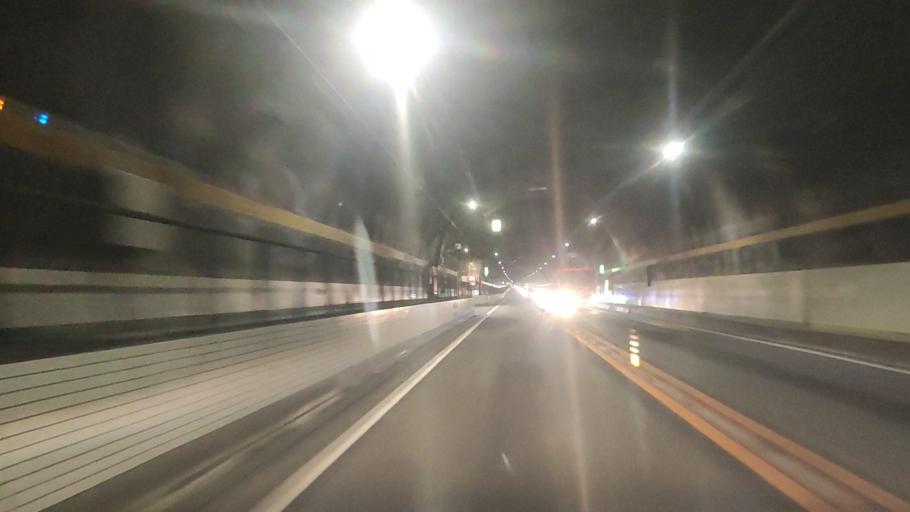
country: JP
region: Nagasaki
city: Obita
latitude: 32.7879
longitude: 129.8825
